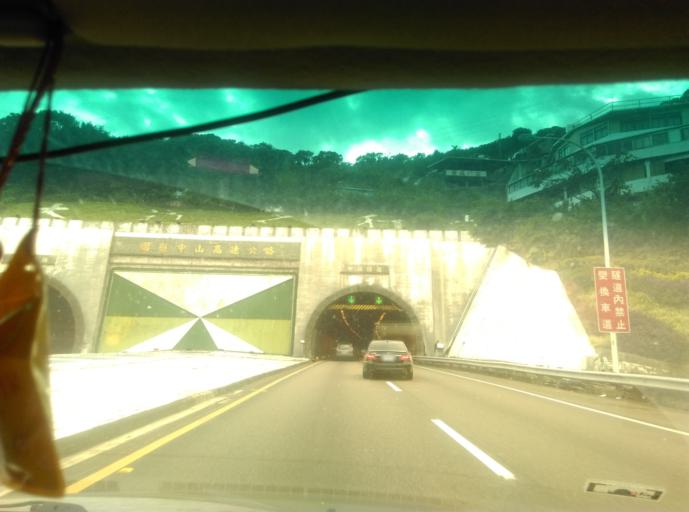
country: TW
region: Taiwan
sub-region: Keelung
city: Keelung
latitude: 25.1228
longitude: 121.7356
